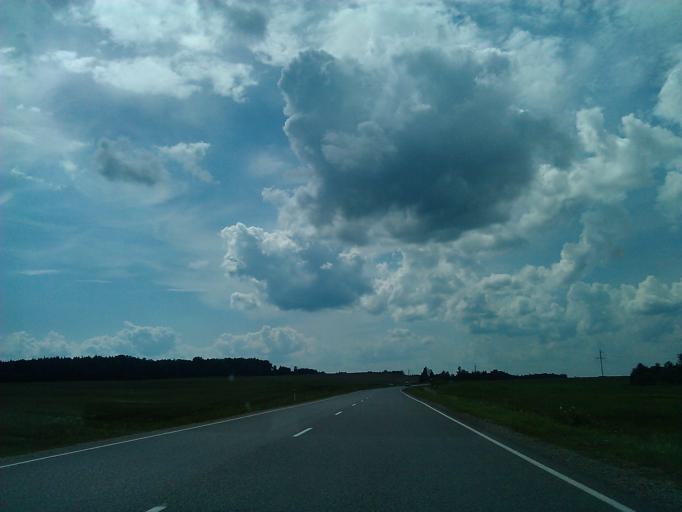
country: LV
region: Jaunpils
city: Jaunpils
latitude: 56.6627
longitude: 23.0126
